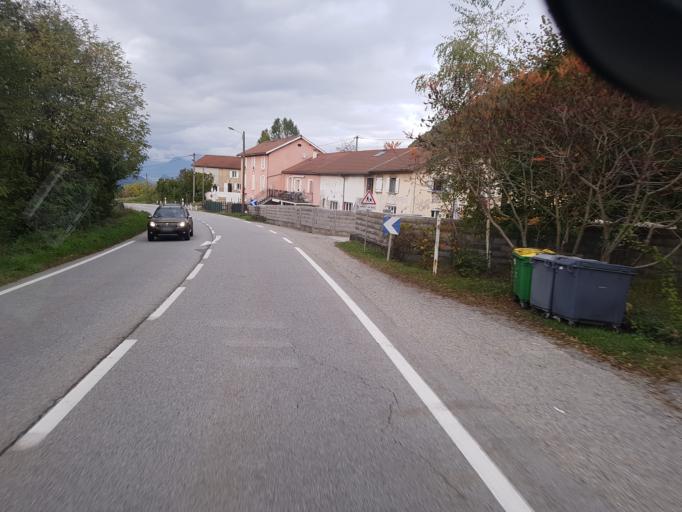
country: FR
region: Rhone-Alpes
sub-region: Departement de l'Isere
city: Vif
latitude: 45.0297
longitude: 5.6641
